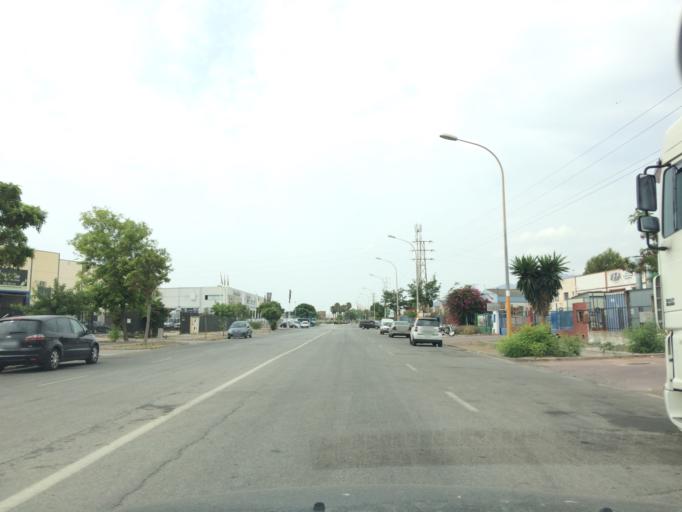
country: ES
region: Andalusia
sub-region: Provincia de Malaga
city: Malaga
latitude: 36.6976
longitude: -4.4835
